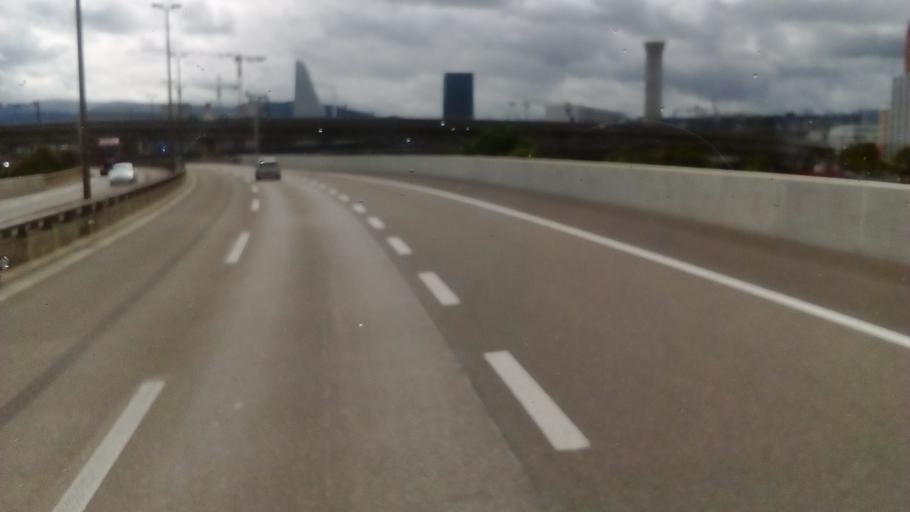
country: DE
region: Baden-Wuerttemberg
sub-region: Freiburg Region
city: Weil am Rhein
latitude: 47.5761
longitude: 7.5992
